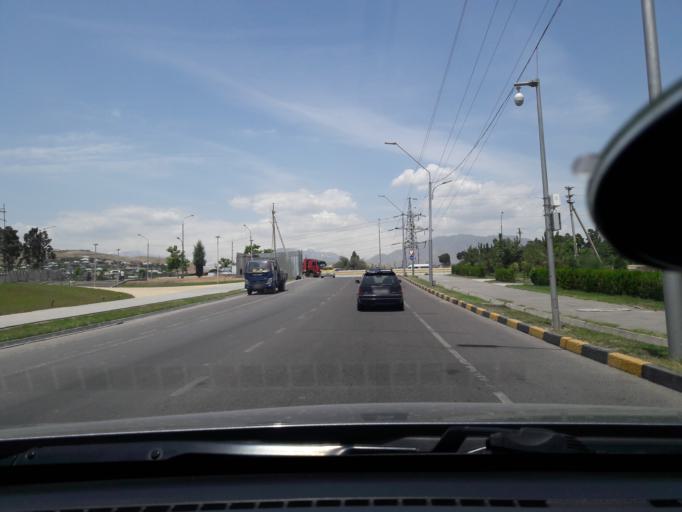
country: TJ
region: Dushanbe
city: Dushanbe
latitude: 38.5964
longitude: 68.7657
